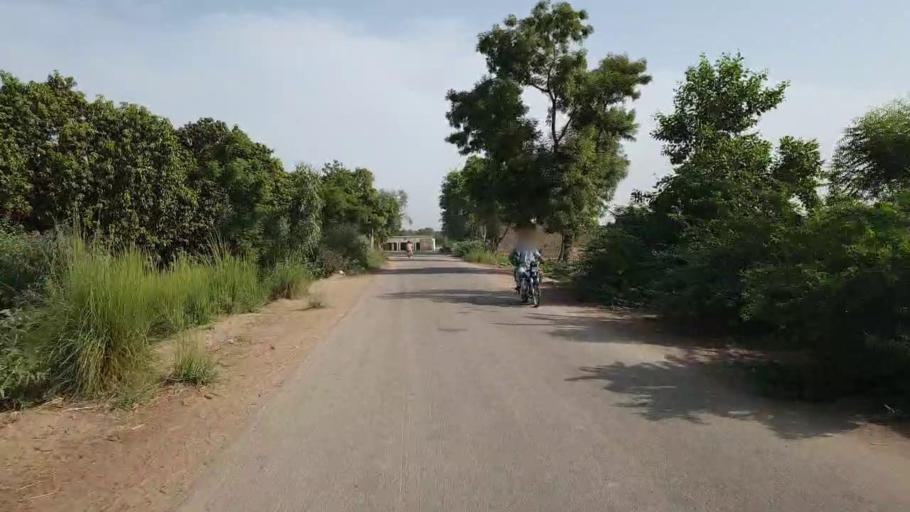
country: PK
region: Sindh
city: Sakrand
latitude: 26.2457
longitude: 68.2846
